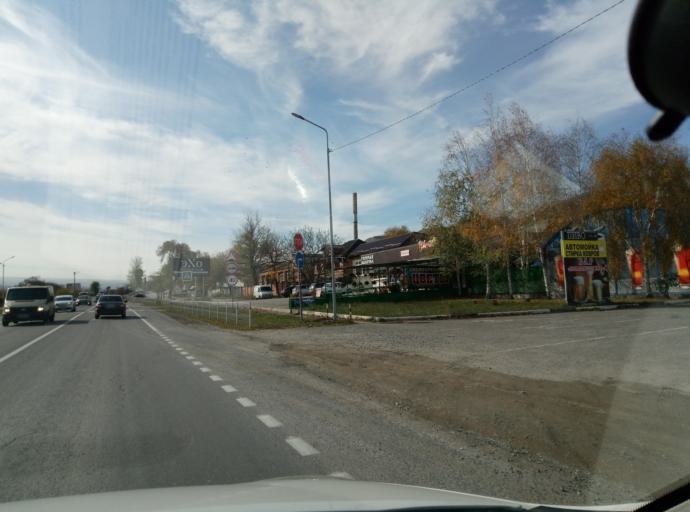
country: RU
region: Stavropol'skiy
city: Yasnaya Polyana
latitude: 43.9627
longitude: 42.7721
